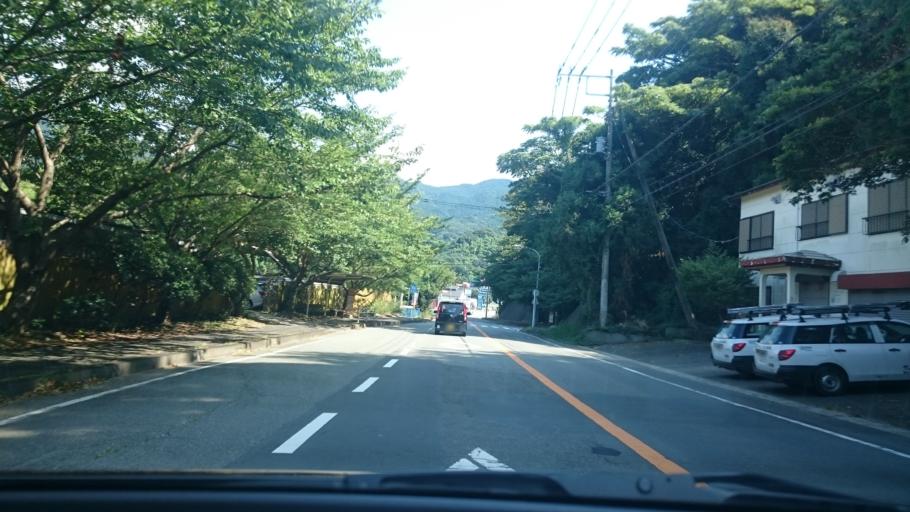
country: JP
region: Shizuoka
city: Heda
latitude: 34.8936
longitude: 138.7696
